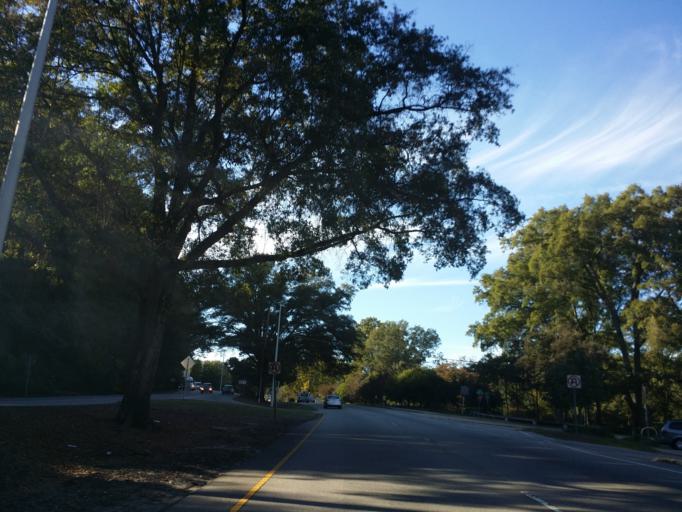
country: US
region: North Carolina
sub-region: Wake County
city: West Raleigh
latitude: 35.7782
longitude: -78.6631
